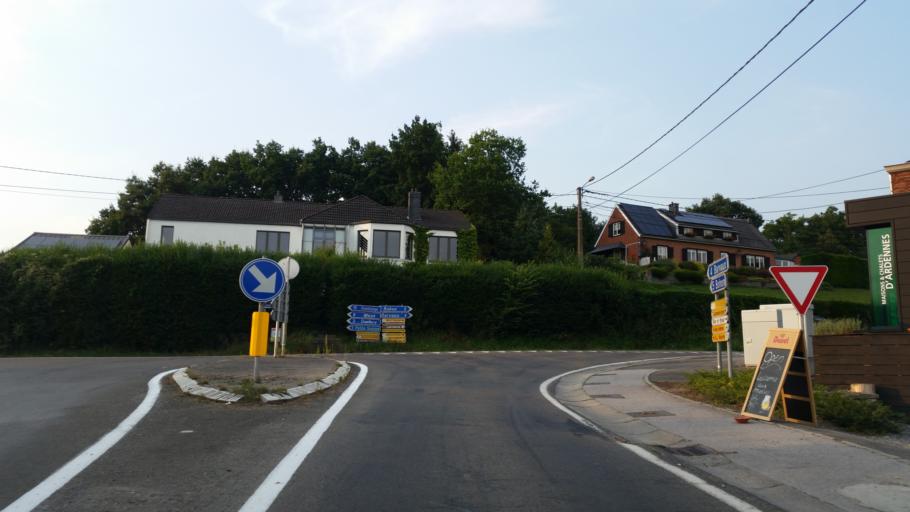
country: BE
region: Wallonia
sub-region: Province du Luxembourg
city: Durbuy
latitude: 50.3378
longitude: 5.4375
